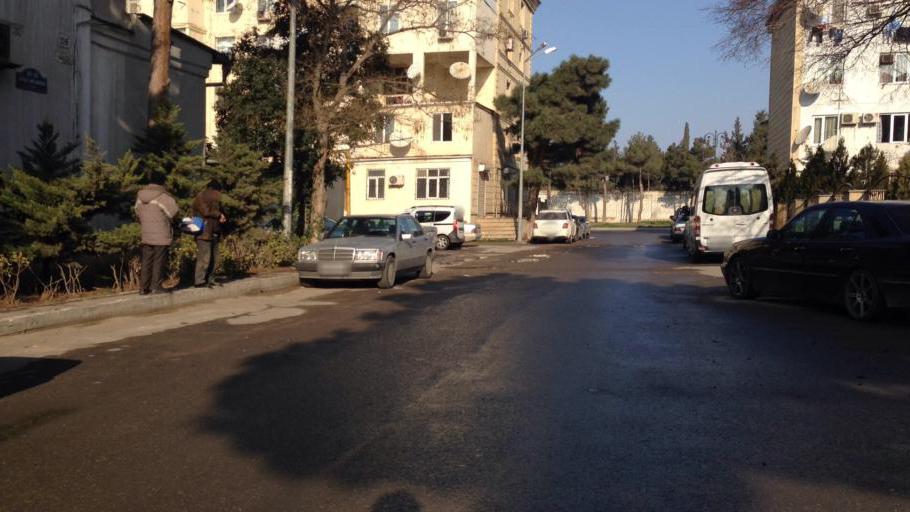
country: AZ
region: Baki
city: Baku
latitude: 40.4038
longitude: 49.8520
